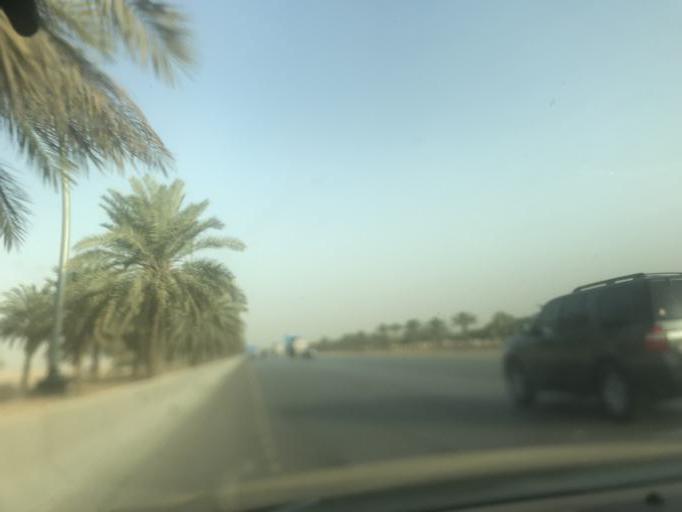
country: SA
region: Ar Riyad
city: Riyadh
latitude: 24.8787
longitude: 46.7243
